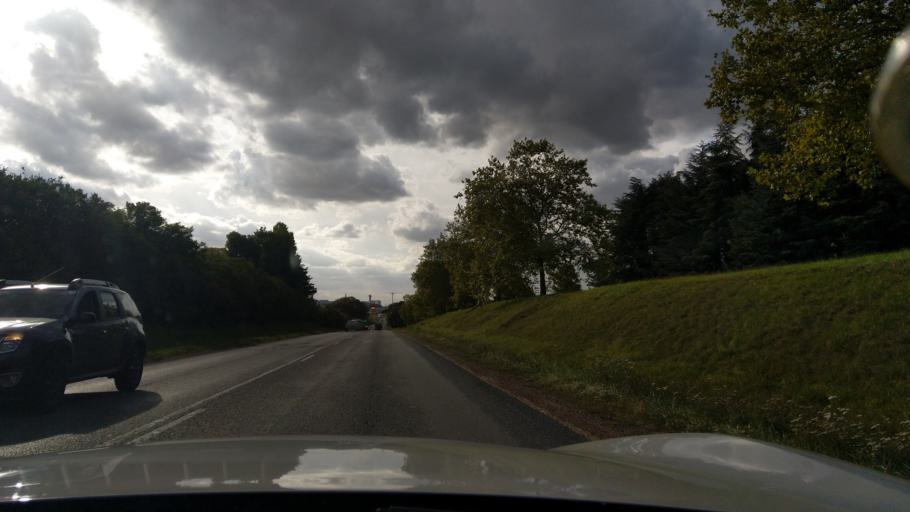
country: FR
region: Ile-de-France
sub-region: Departement de Seine-et-Marne
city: Mitry-Mory
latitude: 49.0136
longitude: 2.6005
